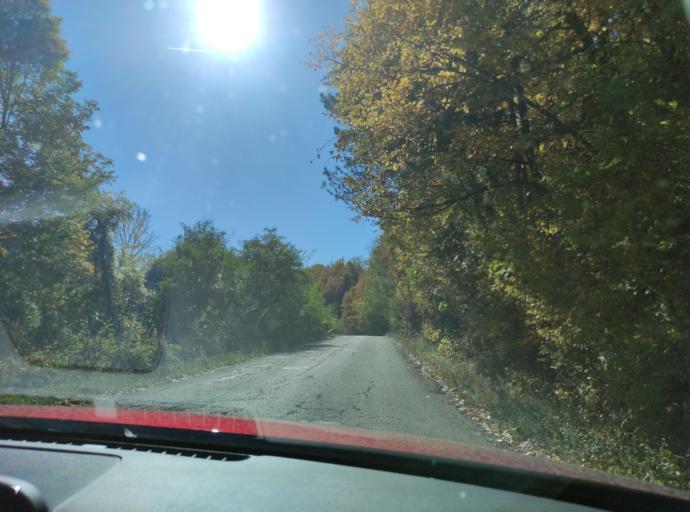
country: BG
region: Montana
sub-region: Obshtina Chiprovtsi
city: Chiprovtsi
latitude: 43.4119
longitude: 22.9398
